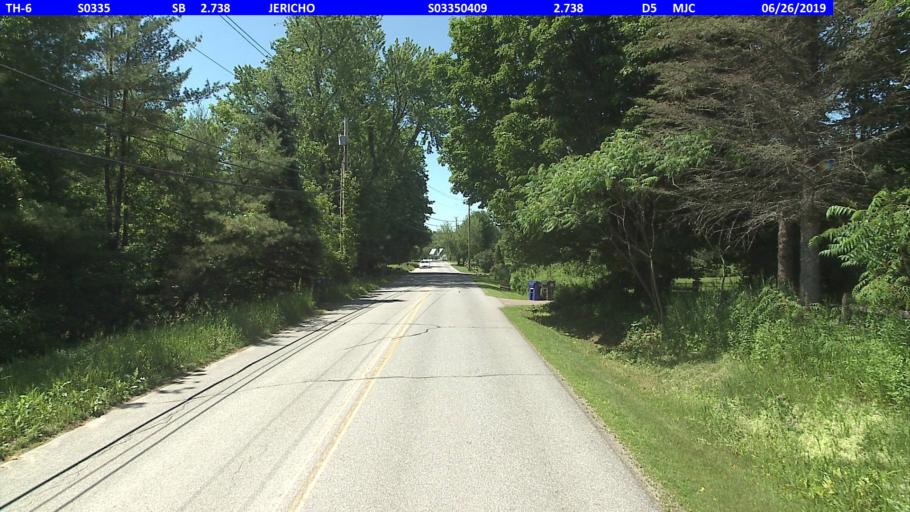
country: US
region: Vermont
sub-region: Chittenden County
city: Jericho
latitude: 44.4988
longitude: -72.9989
